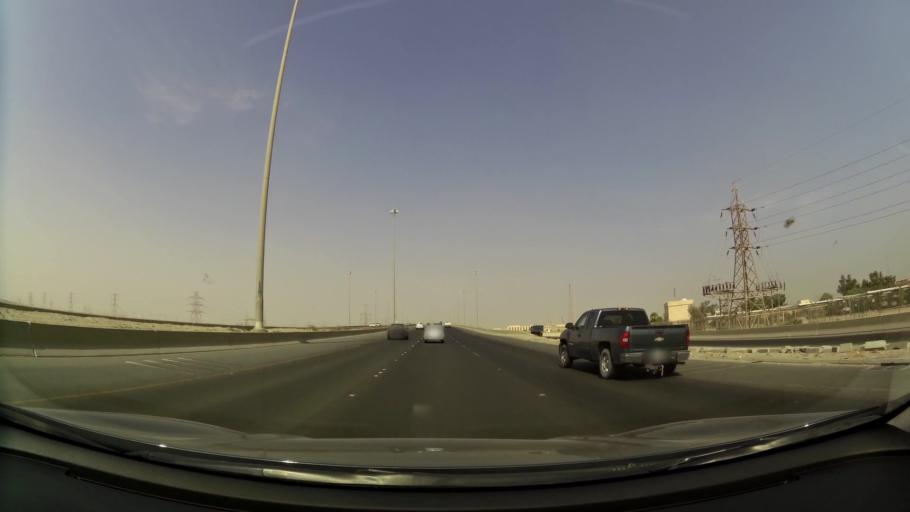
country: KW
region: Al Ahmadi
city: Al Fahahil
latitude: 29.0331
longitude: 48.1206
